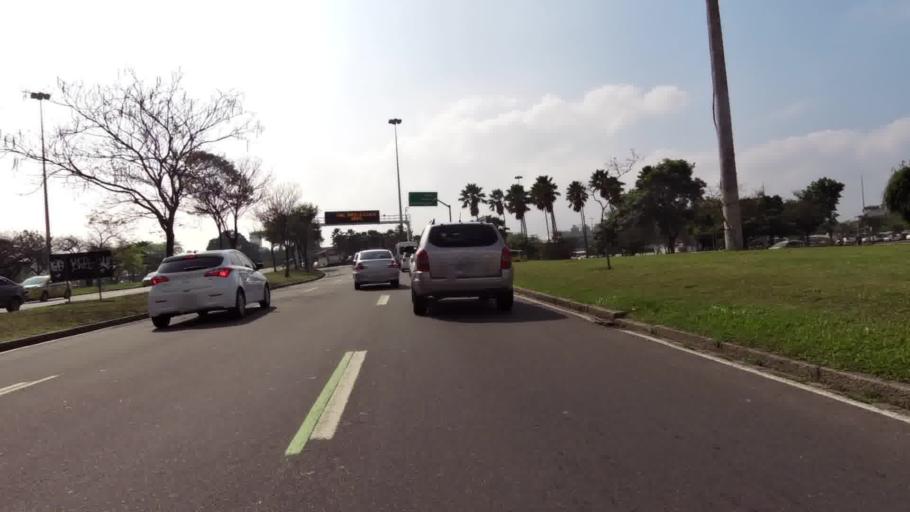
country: BR
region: Rio de Janeiro
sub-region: Rio De Janeiro
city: Rio de Janeiro
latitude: -22.9119
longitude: -43.1703
